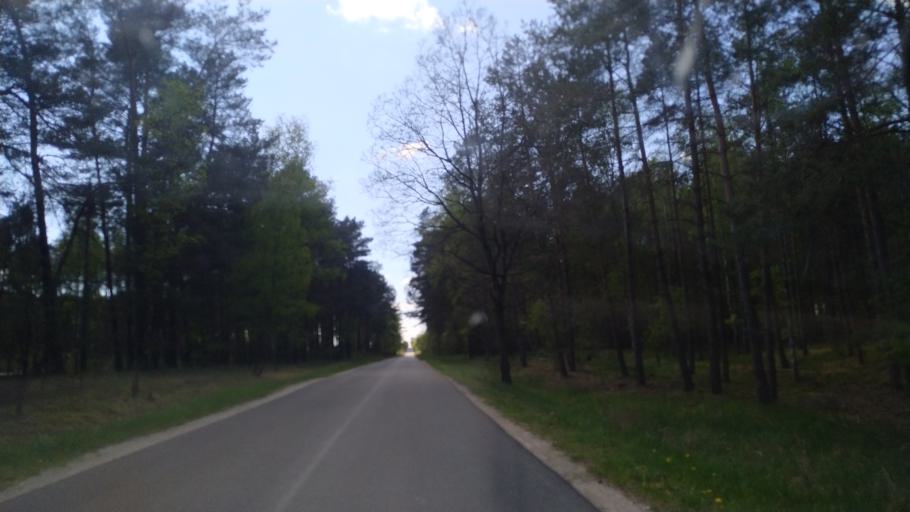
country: PL
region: Greater Poland Voivodeship
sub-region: Powiat pilski
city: Pila
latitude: 53.2429
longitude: 16.7043
